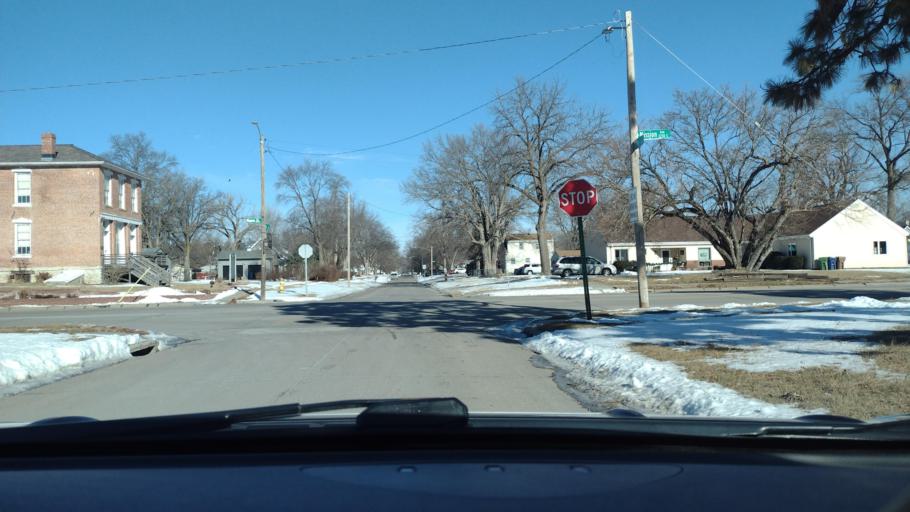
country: US
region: Nebraska
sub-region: Sarpy County
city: Bellevue
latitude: 41.1363
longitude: -95.8909
